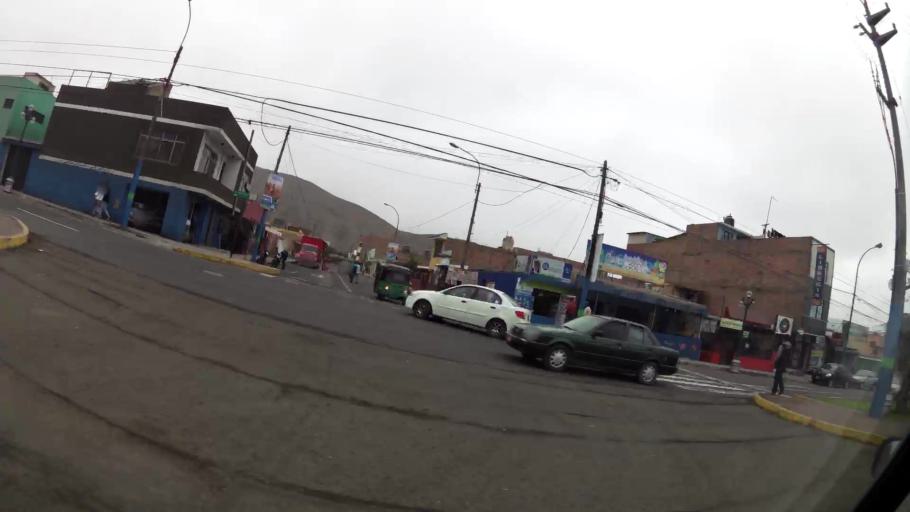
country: PE
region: Lima
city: Ventanilla
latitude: -11.8727
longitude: -77.1244
